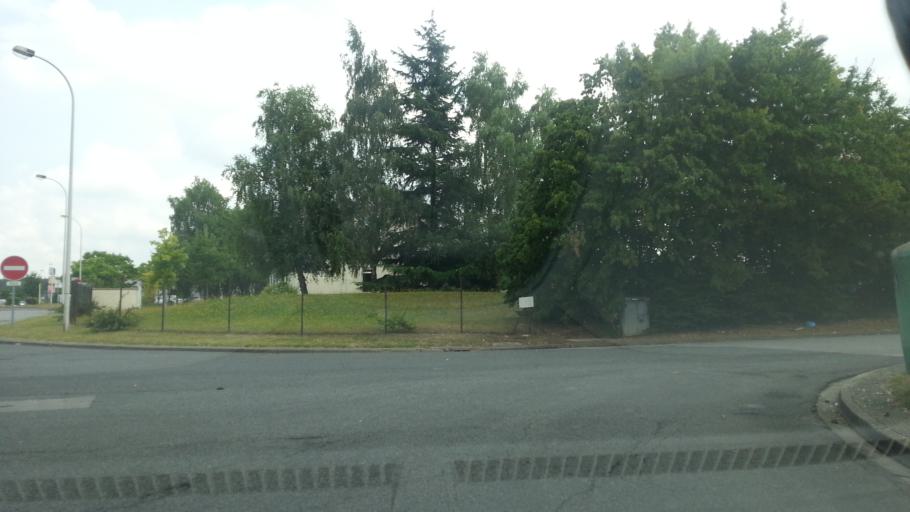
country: FR
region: Picardie
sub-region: Departement de l'Oise
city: Creil
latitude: 49.2433
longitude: 2.4658
